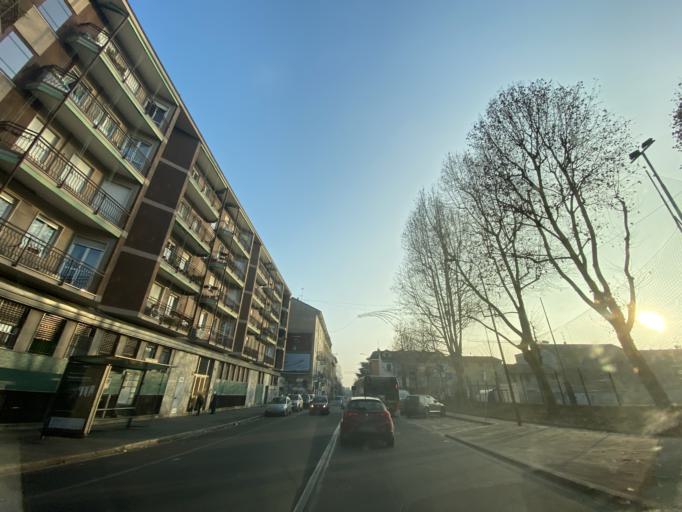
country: IT
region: Lombardy
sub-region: Citta metropolitana di Milano
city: Bresso
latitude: 45.5021
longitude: 9.1780
